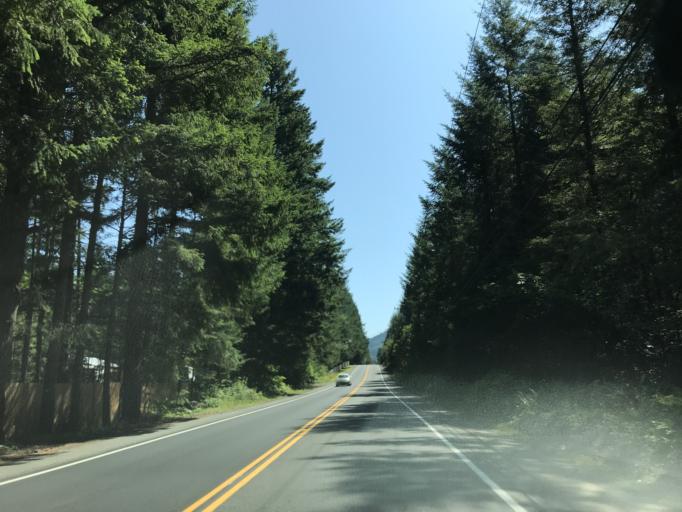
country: US
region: Washington
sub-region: King County
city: Ravensdale
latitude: 47.3580
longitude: -121.9204
